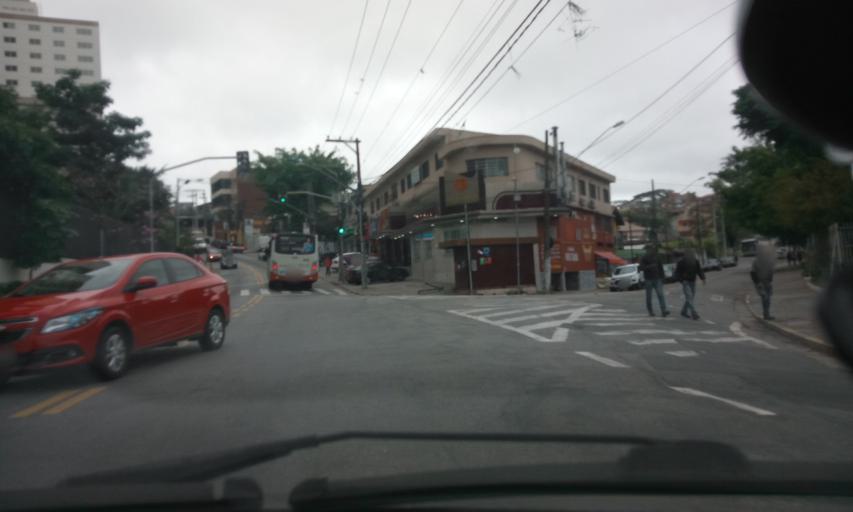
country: BR
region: Sao Paulo
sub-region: Taboao Da Serra
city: Taboao da Serra
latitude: -23.6187
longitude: -46.7741
